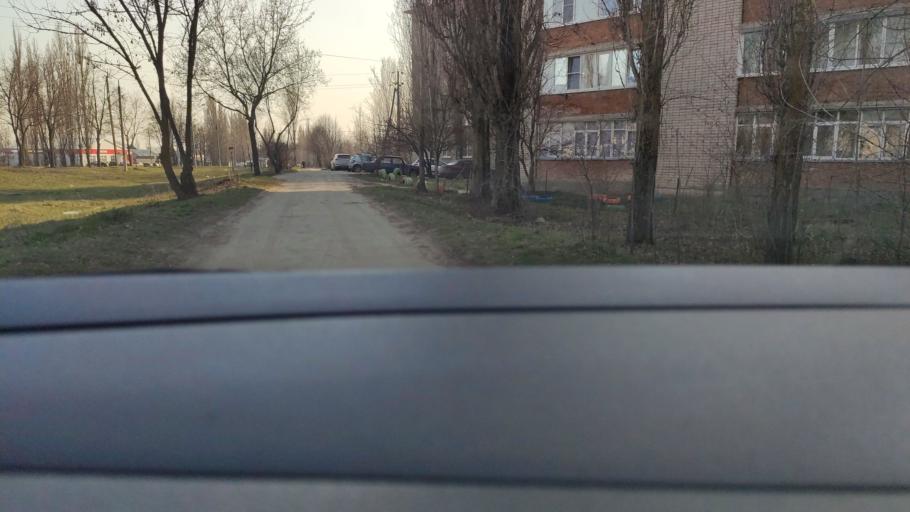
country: RU
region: Voronezj
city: Maslovka
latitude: 51.5862
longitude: 39.3207
